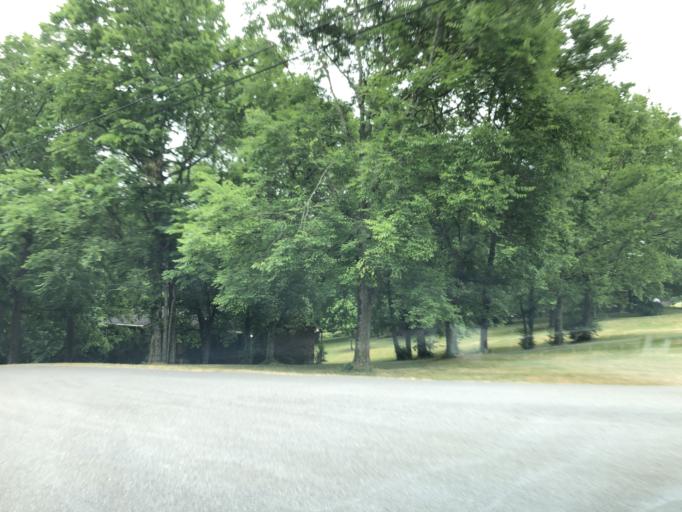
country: US
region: Tennessee
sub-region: Davidson County
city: Goodlettsville
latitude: 36.2862
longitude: -86.7377
